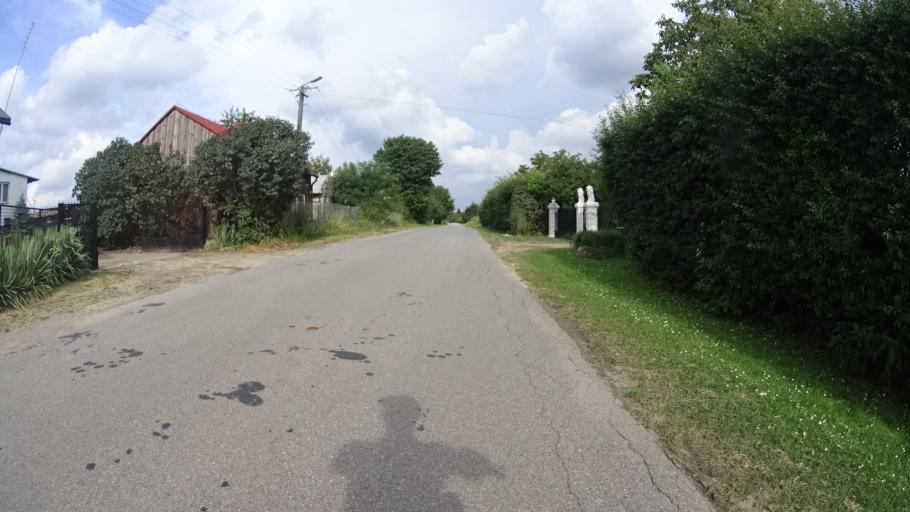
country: PL
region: Masovian Voivodeship
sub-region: Powiat grojecki
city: Goszczyn
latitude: 51.6965
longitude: 20.8301
